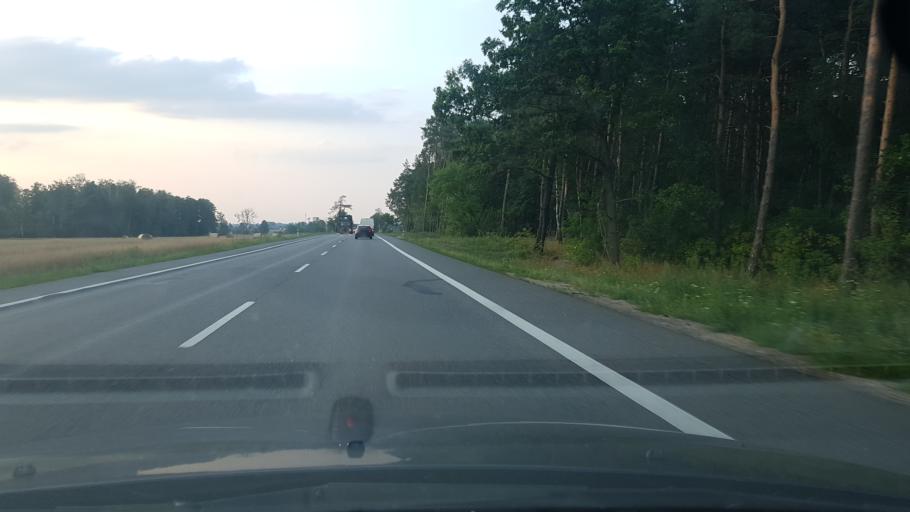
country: PL
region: Masovian Voivodeship
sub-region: Powiat mlawski
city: Strzegowo
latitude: 52.9237
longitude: 20.2861
